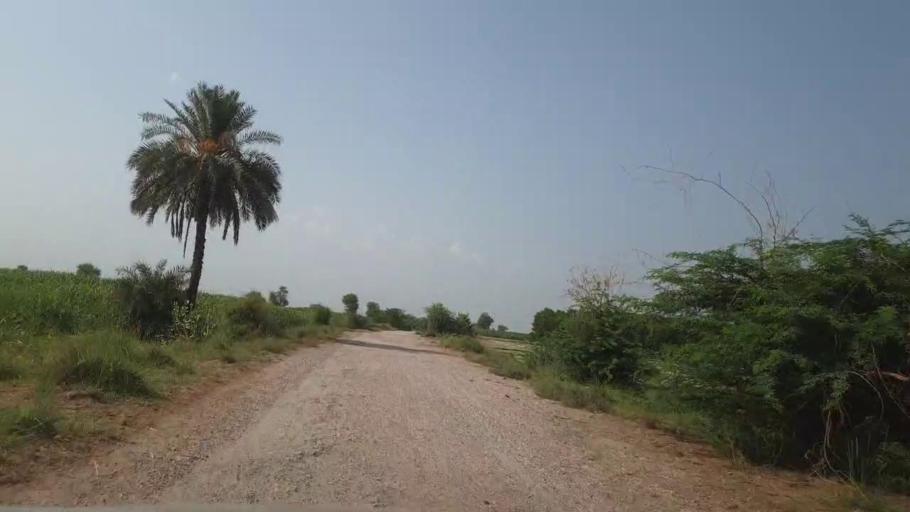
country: PK
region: Sindh
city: Pano Aqil
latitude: 27.7803
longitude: 69.1601
